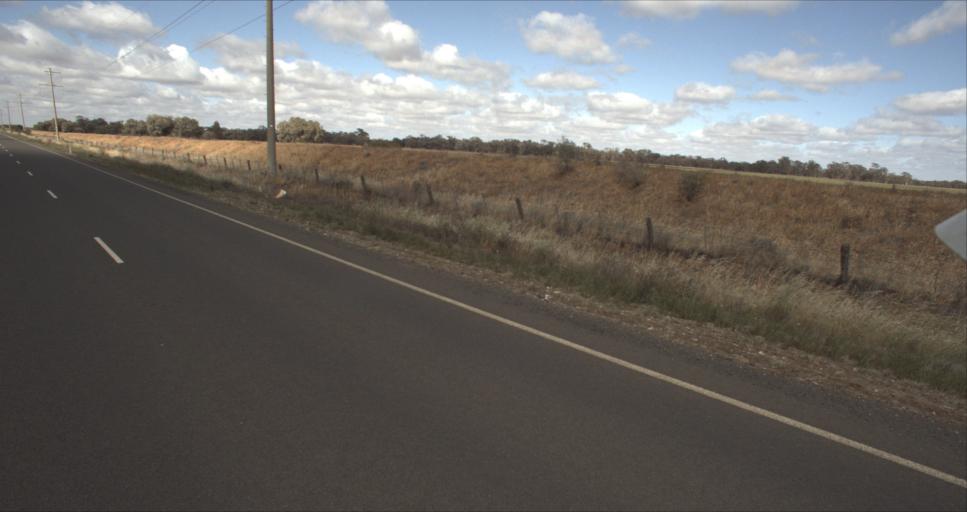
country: AU
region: New South Wales
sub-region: Murrumbidgee Shire
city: Darlington Point
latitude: -34.5375
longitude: 146.1728
